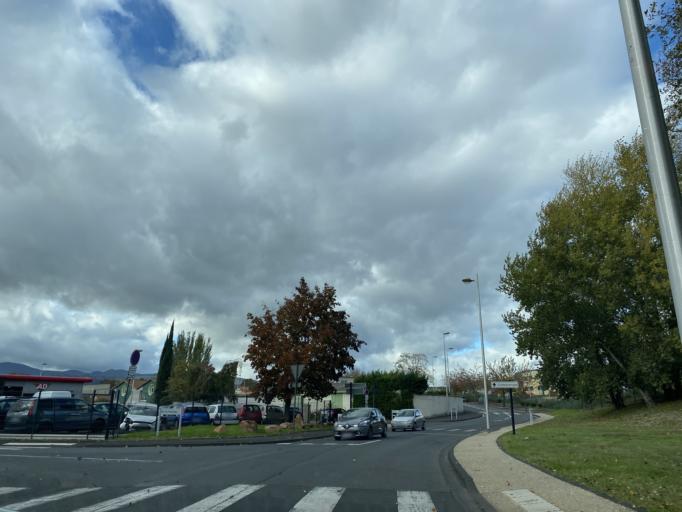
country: FR
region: Auvergne
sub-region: Departement du Puy-de-Dome
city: Aubiere
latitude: 45.7676
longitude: 3.1324
